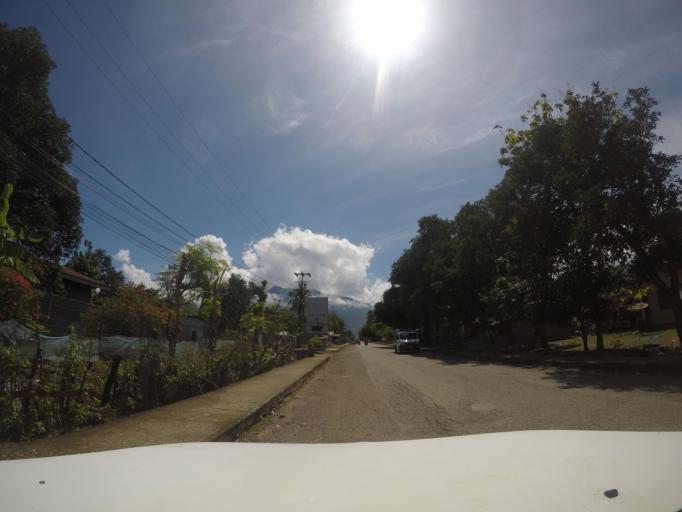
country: TL
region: Bobonaro
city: Maliana
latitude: -8.9904
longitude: 125.2025
